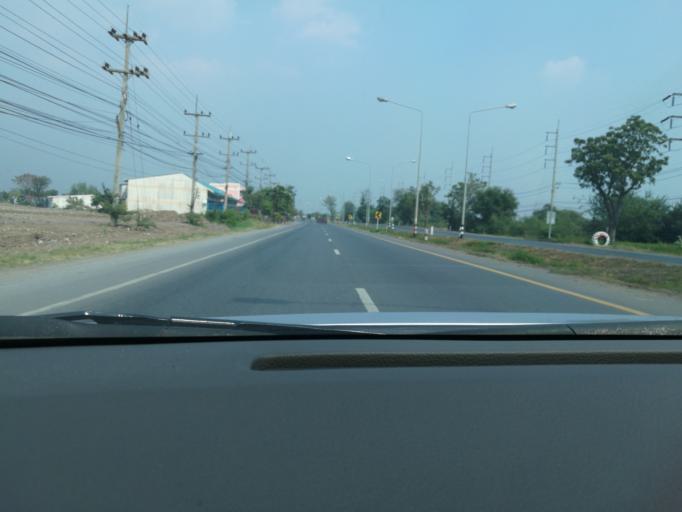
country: TH
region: Lop Buri
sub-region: Amphoe Tha Luang
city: Tha Luang
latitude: 15.0875
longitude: 101.0094
